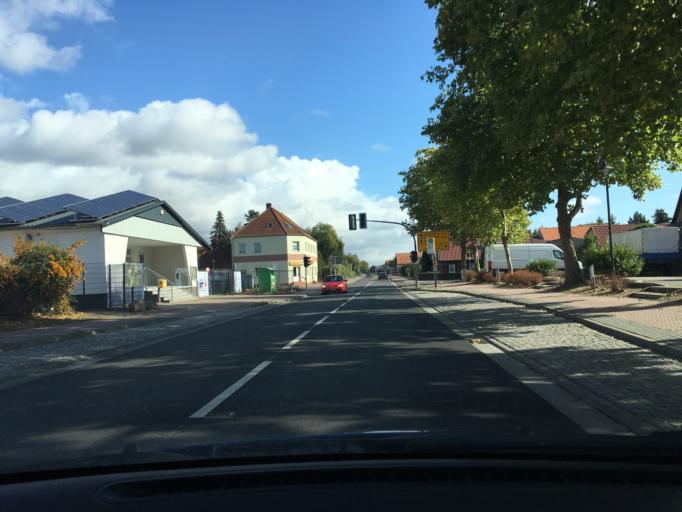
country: DE
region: Saxony-Anhalt
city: Pretzier
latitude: 52.8340
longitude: 11.2606
